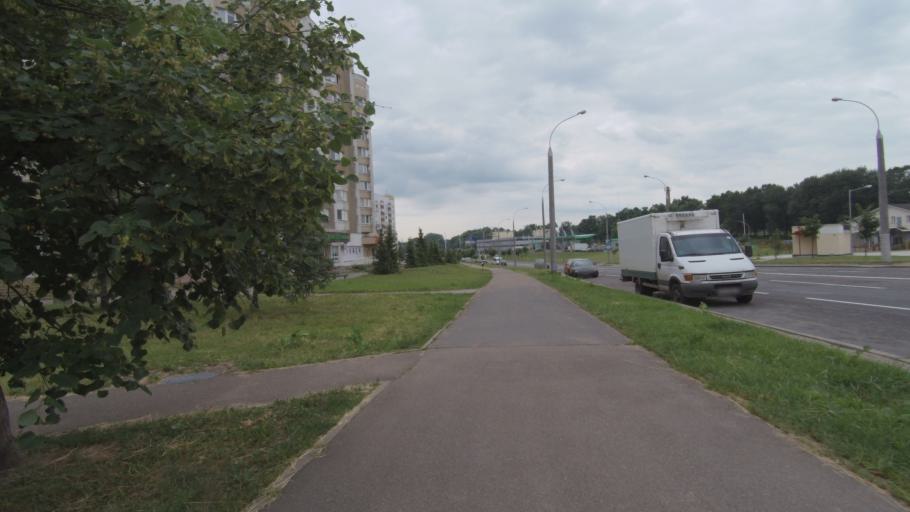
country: BY
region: Minsk
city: Syenitsa
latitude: 53.8456
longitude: 27.5595
